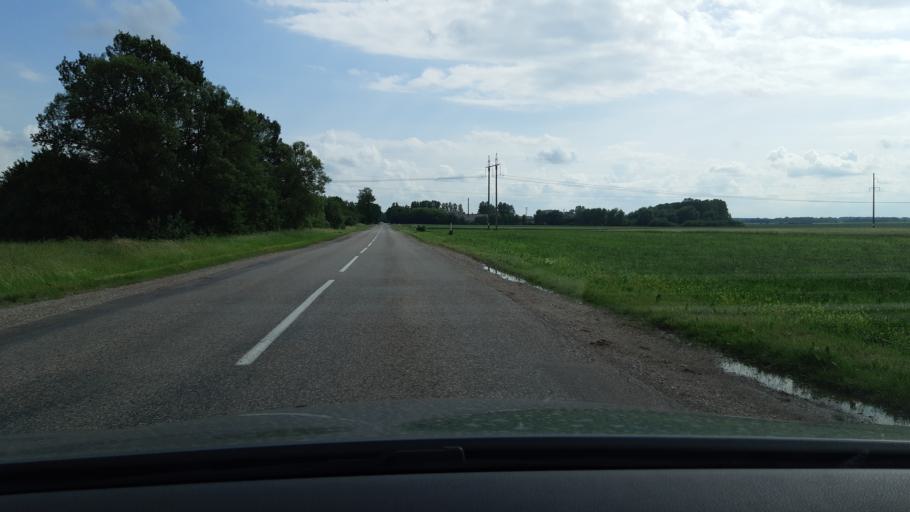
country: LT
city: Kybartai
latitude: 54.6264
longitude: 22.7533
